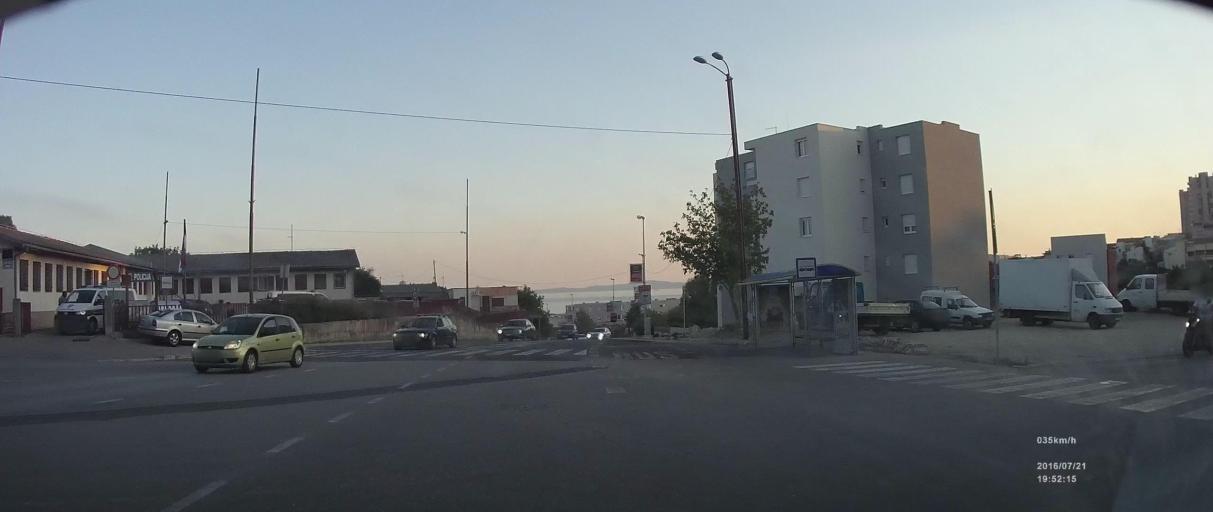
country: HR
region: Splitsko-Dalmatinska
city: Vranjic
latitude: 43.5060
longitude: 16.4787
